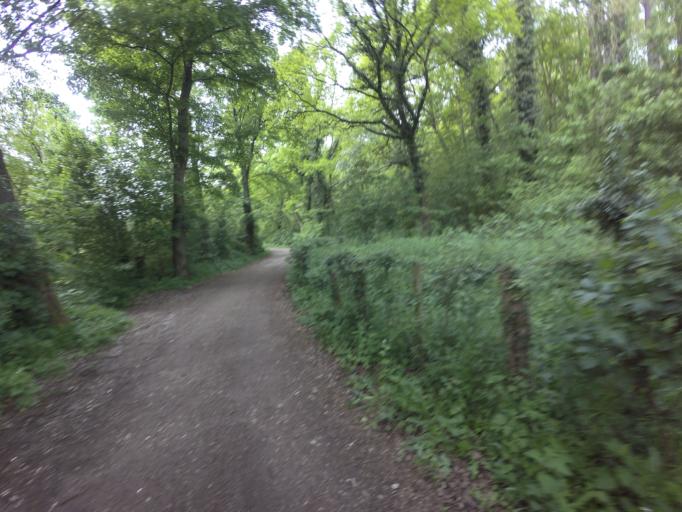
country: NL
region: Limburg
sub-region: Gemeente Maastricht
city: Heer
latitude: 50.8203
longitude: 5.7570
